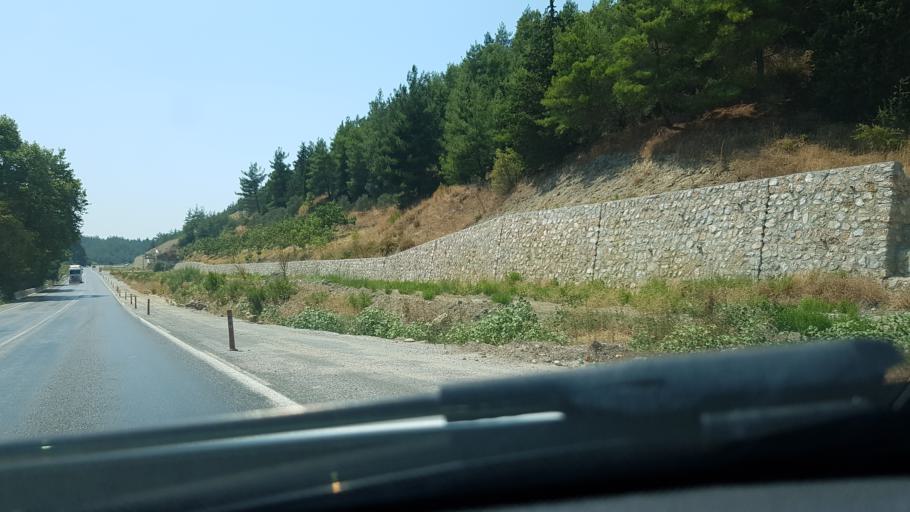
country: TR
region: Aydin
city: Ortaklar
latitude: 37.8863
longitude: 27.4430
